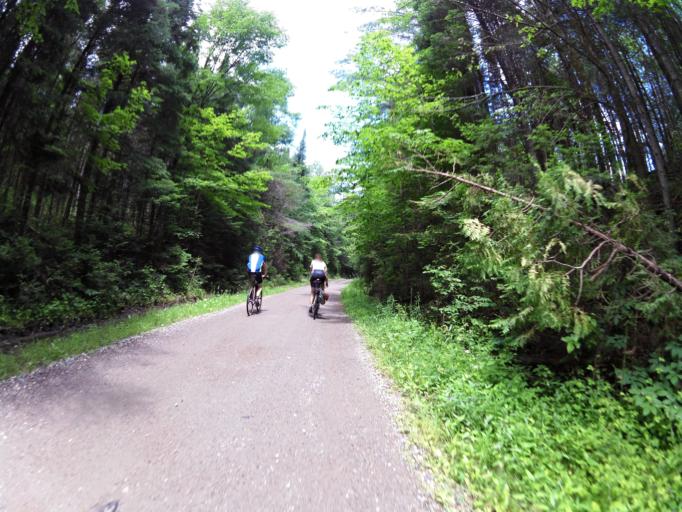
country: CA
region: Ontario
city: Renfrew
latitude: 45.1115
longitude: -76.6969
